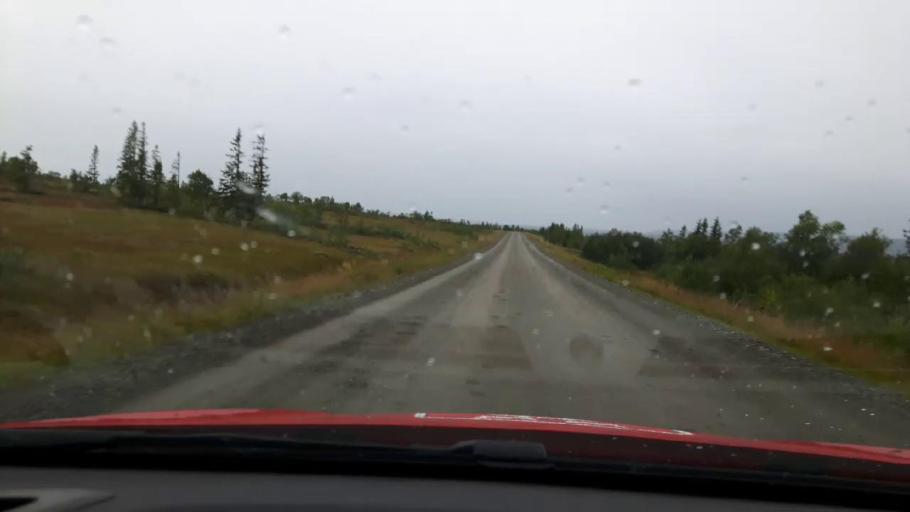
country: NO
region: Nord-Trondelag
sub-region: Meraker
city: Meraker
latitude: 63.6103
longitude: 12.2761
